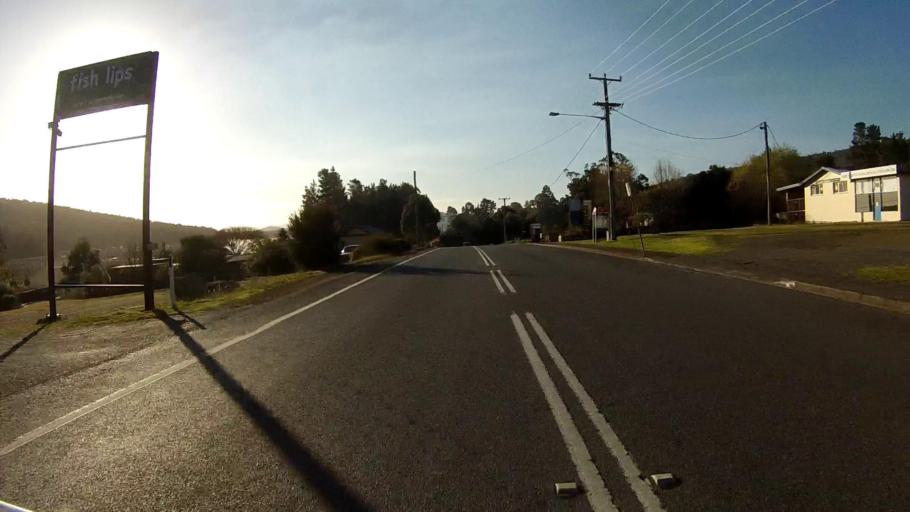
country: AU
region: Tasmania
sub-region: Clarence
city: Sandford
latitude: -43.0560
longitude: 147.8652
